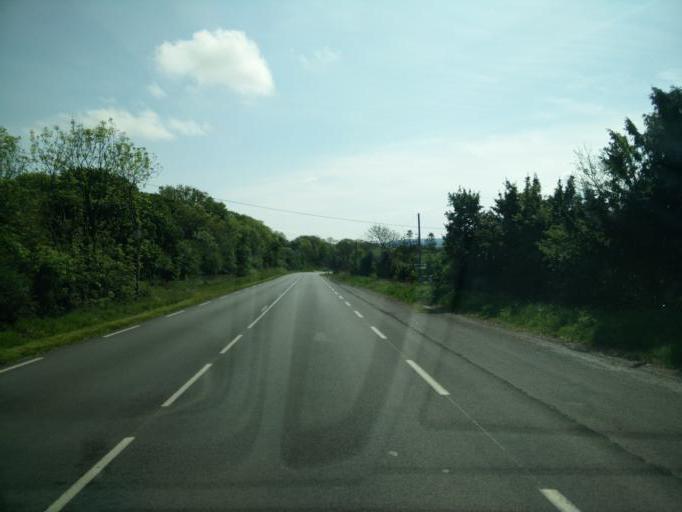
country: FR
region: Brittany
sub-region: Departement du Finistere
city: Telgruc-sur-Mer
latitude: 48.2477
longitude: -4.4010
